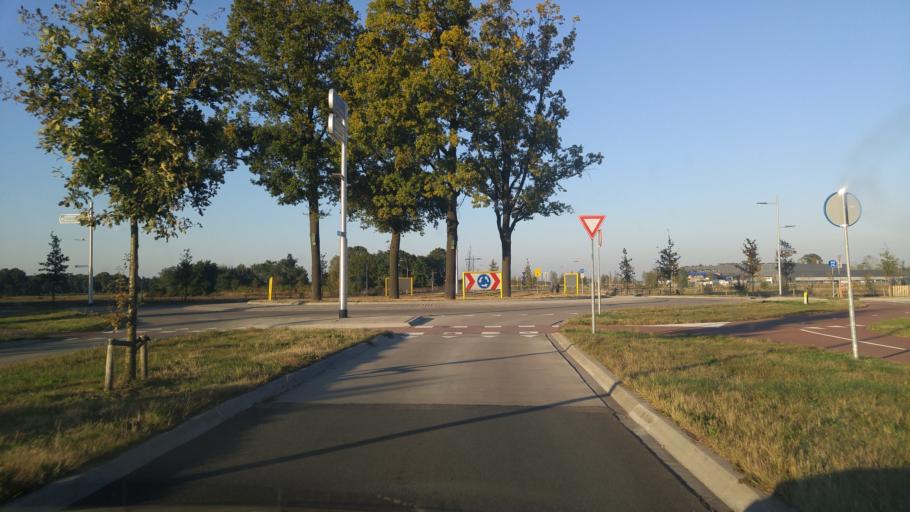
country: NL
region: North Brabant
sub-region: Gemeente Veldhoven
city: Oerle
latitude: 51.4308
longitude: 5.3573
